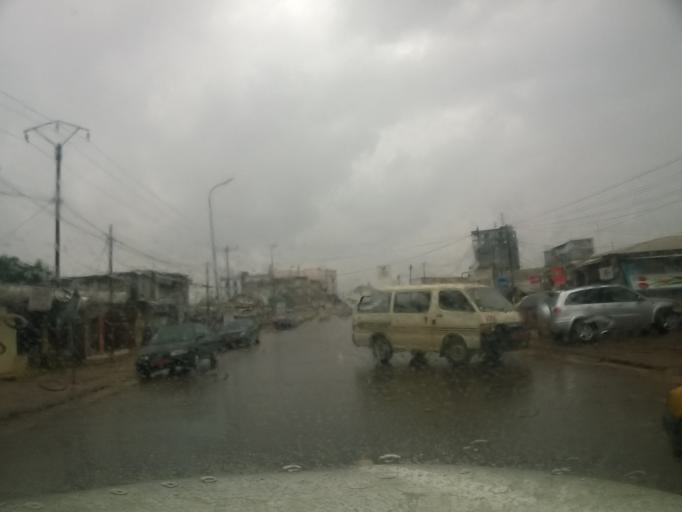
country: CM
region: Centre
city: Yaounde
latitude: 3.8704
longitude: 11.5341
